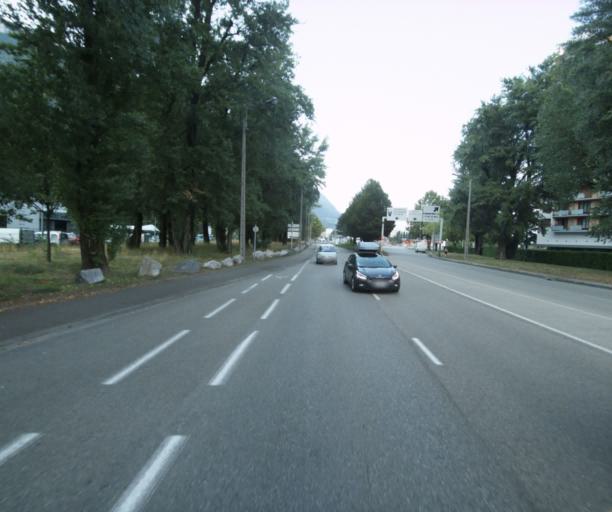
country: FR
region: Rhone-Alpes
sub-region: Departement de l'Isere
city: Fontaine
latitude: 45.1943
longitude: 5.6757
